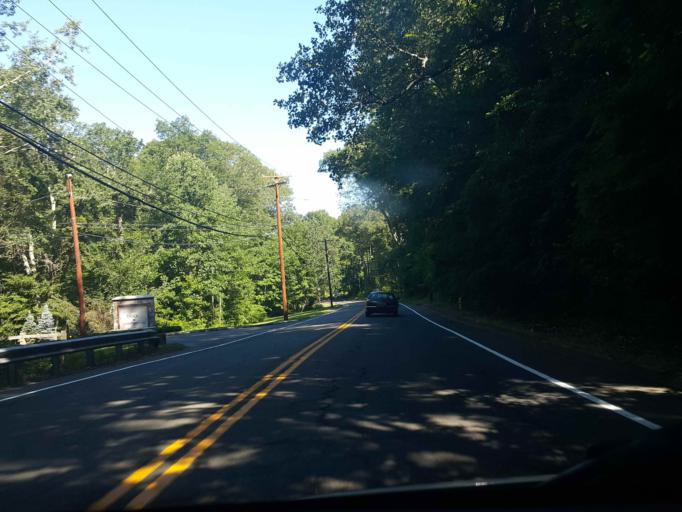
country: US
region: Connecticut
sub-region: New Haven County
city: North Branford
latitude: 41.3165
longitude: -72.7507
